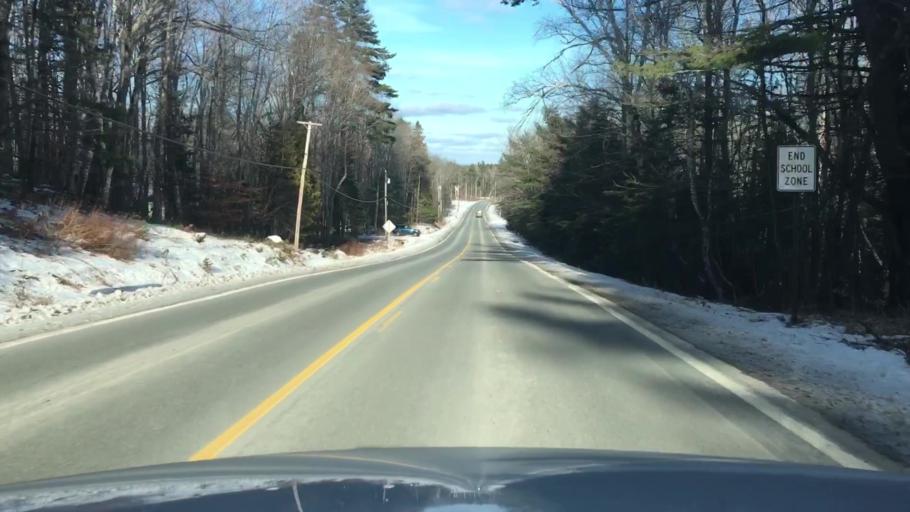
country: US
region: Maine
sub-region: Penobscot County
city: Holden
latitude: 44.7464
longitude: -68.6145
